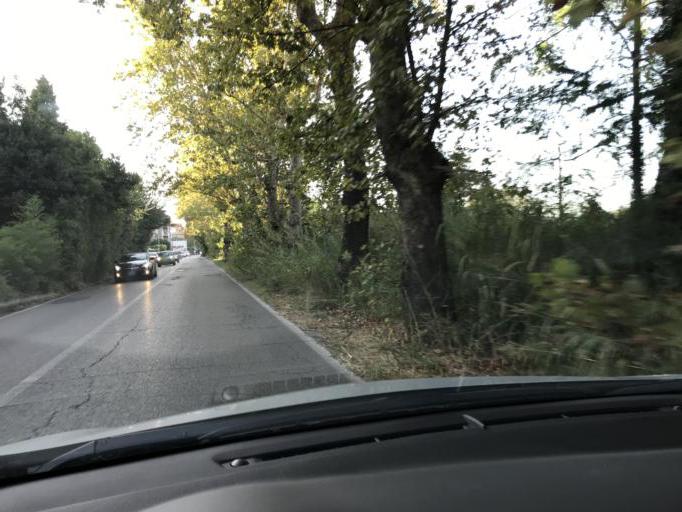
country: IT
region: Latium
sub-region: Provincia di Viterbo
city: Orte Scalo
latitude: 42.4446
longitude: 12.4002
